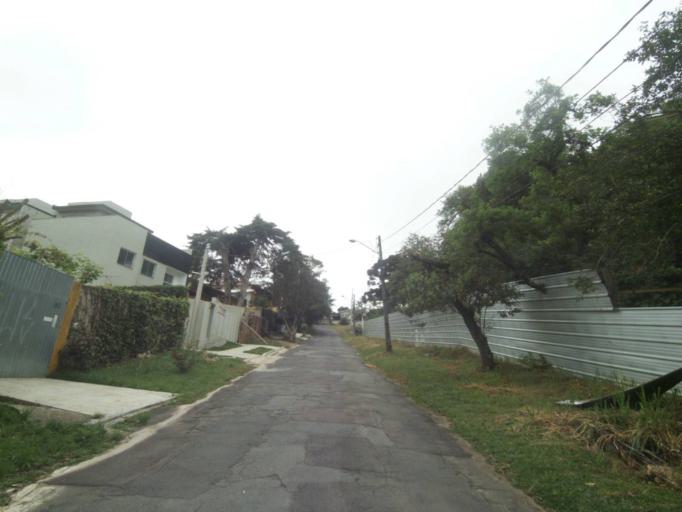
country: BR
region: Parana
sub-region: Curitiba
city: Curitiba
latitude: -25.3937
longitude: -49.2750
